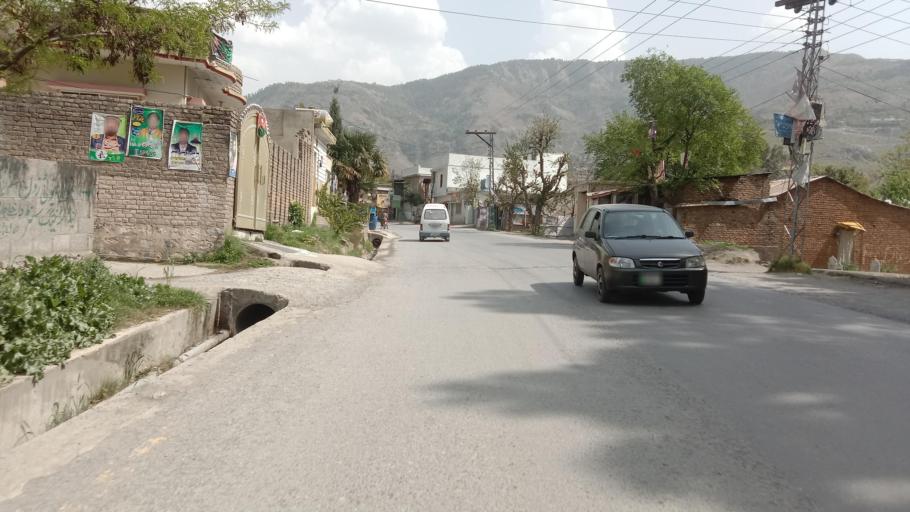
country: PK
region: Khyber Pakhtunkhwa
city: Abbottabad
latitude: 34.1387
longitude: 73.2771
